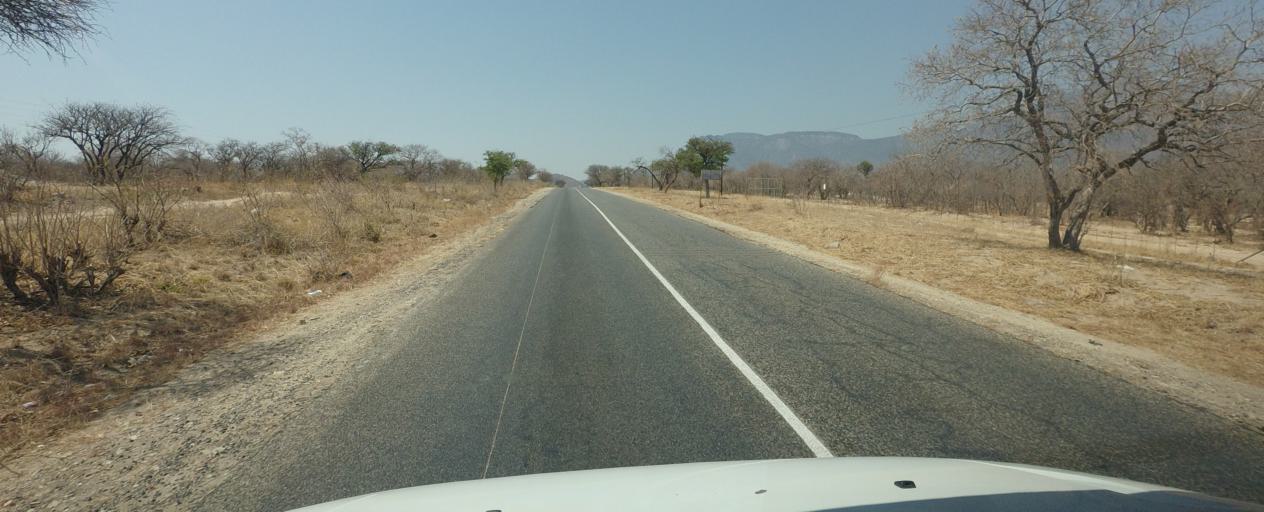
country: ZA
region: Limpopo
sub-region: Mopani District Municipality
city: Hoedspruit
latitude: -24.4799
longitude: 30.8852
